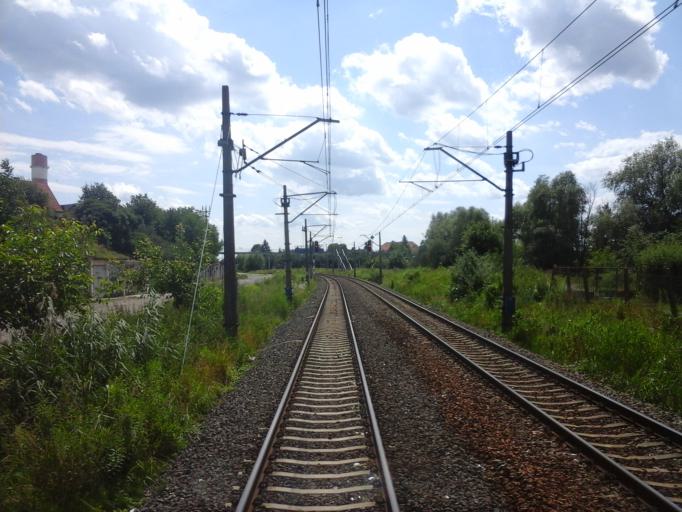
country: PL
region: West Pomeranian Voivodeship
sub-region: Szczecin
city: Szczecin
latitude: 53.3960
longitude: 14.5208
